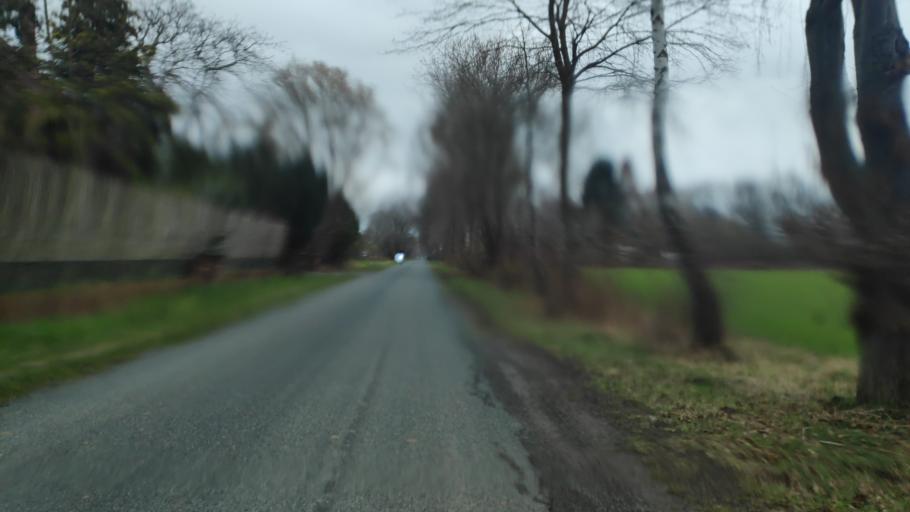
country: DE
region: North Rhine-Westphalia
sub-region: Regierungsbezirk Detmold
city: Hille
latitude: 52.3749
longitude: 8.7735
